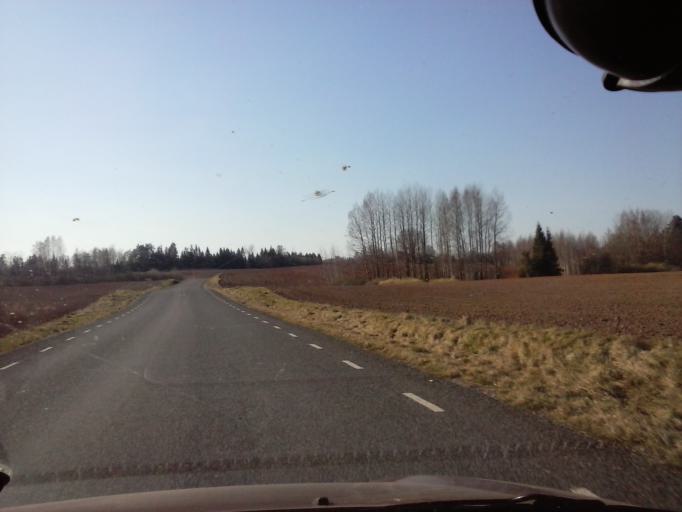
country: EE
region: Tartu
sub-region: UElenurme vald
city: Ulenurme
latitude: 58.1575
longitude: 26.8557
